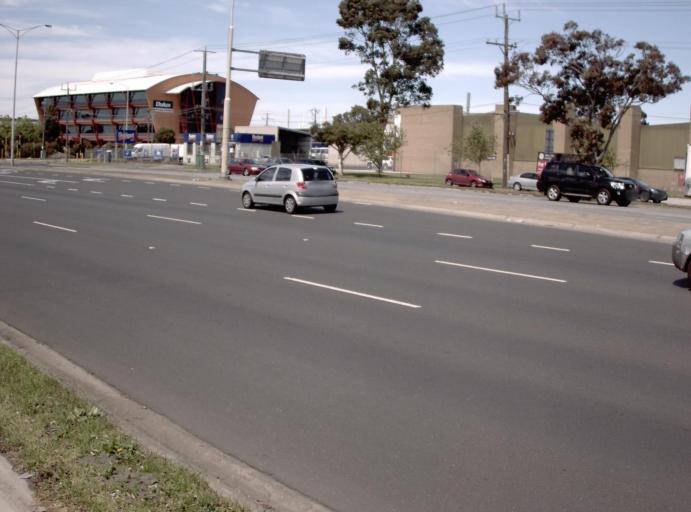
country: AU
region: Victoria
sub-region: Monash
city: Clayton
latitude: -37.9224
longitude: 145.1403
